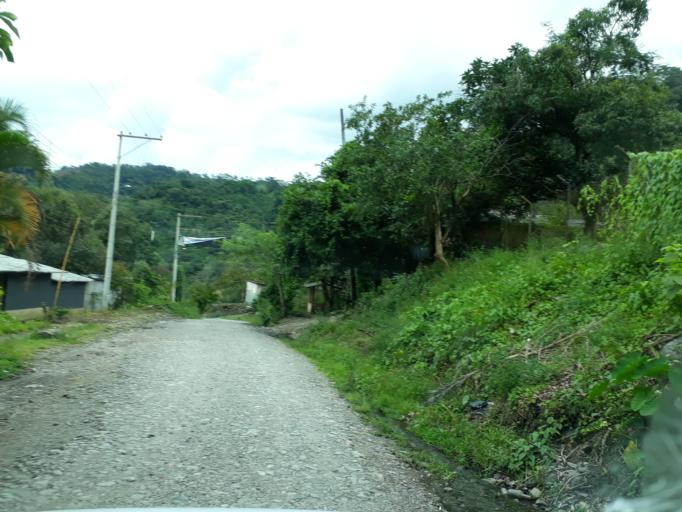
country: CO
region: Boyaca
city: Santa Maria
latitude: 4.7527
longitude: -73.3276
